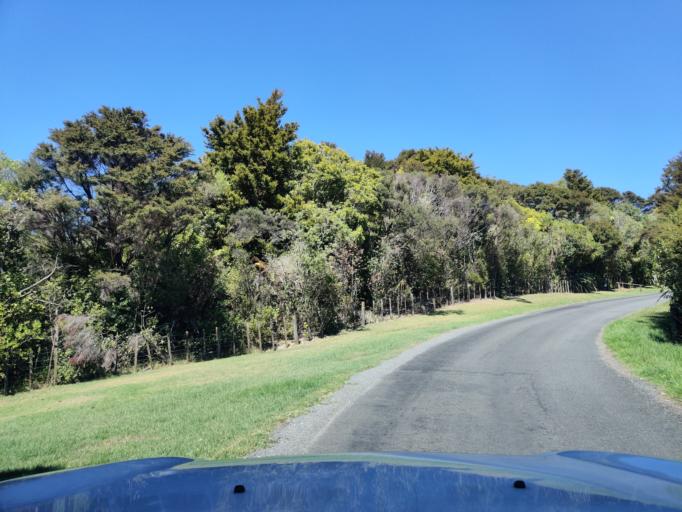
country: NZ
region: Waikato
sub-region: Thames-Coromandel District
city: Thames
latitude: -37.0390
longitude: 175.2946
